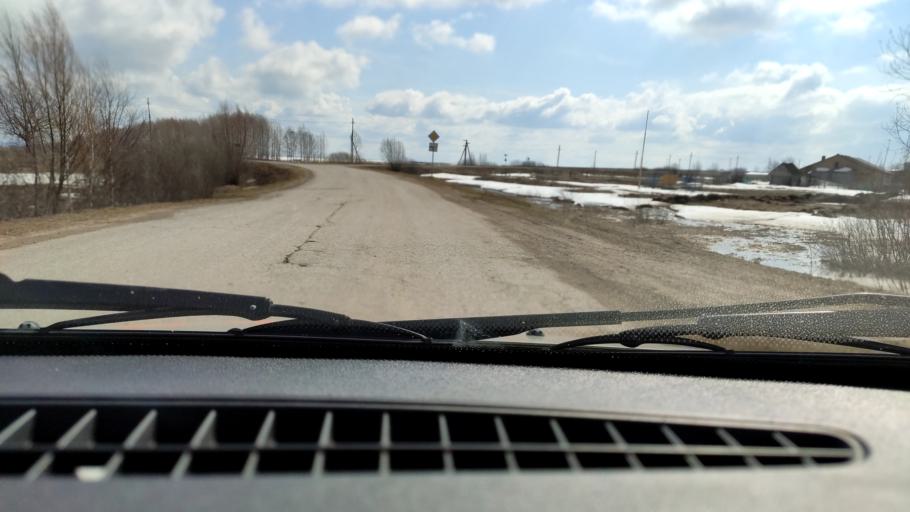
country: RU
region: Bashkortostan
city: Kudeyevskiy
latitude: 54.8518
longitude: 56.7934
